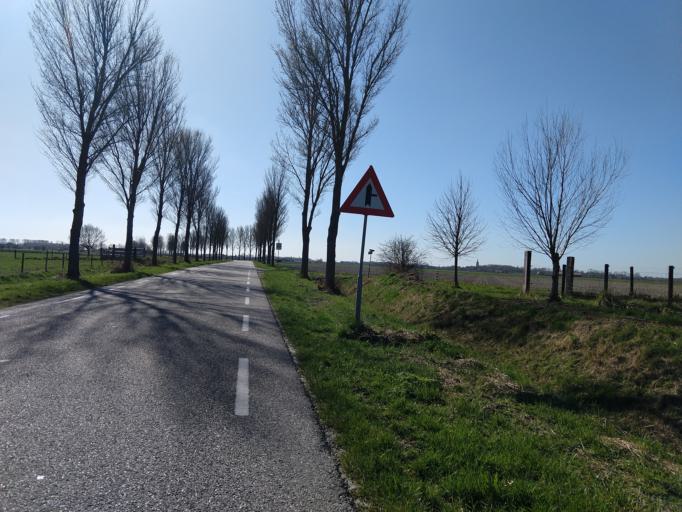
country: NL
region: Zeeland
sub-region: Gemeente Goes
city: Goes
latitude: 51.5006
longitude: 3.9493
